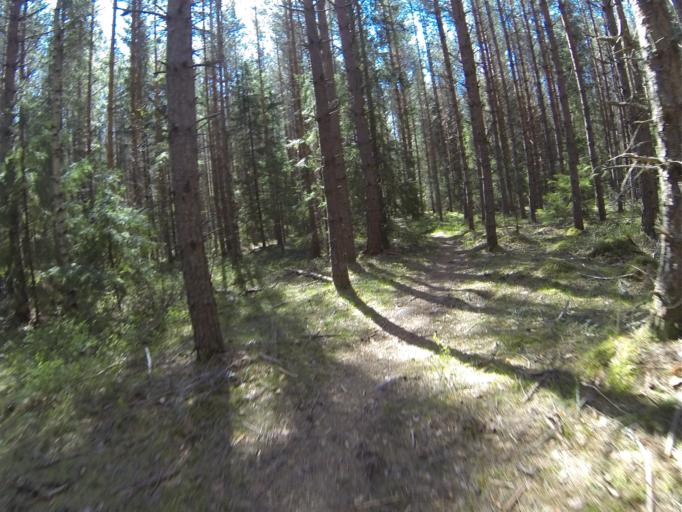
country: FI
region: Varsinais-Suomi
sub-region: Salo
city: Pertteli
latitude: 60.3919
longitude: 23.2104
